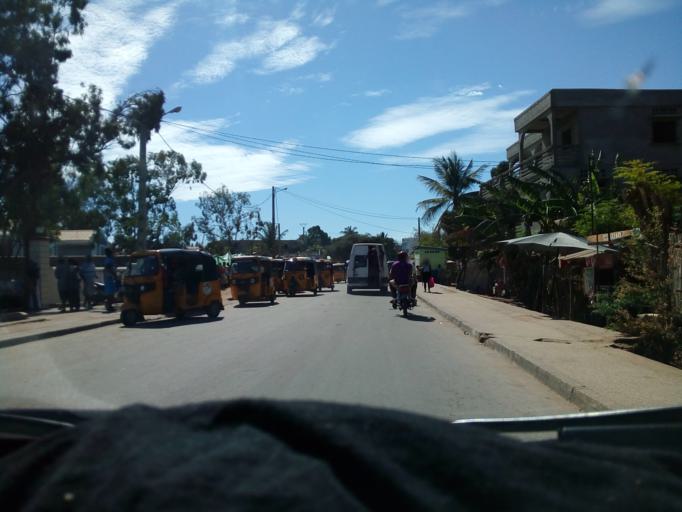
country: MG
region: Boeny
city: Mahajanga
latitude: -15.7086
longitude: 46.3122
